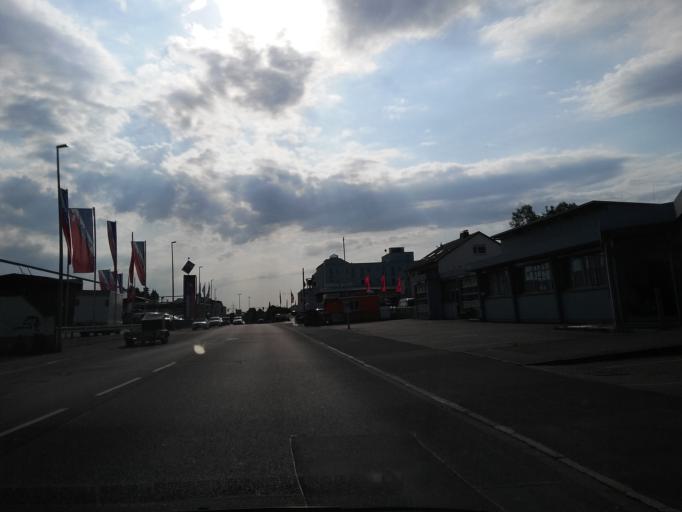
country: DE
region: Baden-Wuerttemberg
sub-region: Regierungsbezirk Stuttgart
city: Backnang
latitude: 48.9367
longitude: 9.4408
